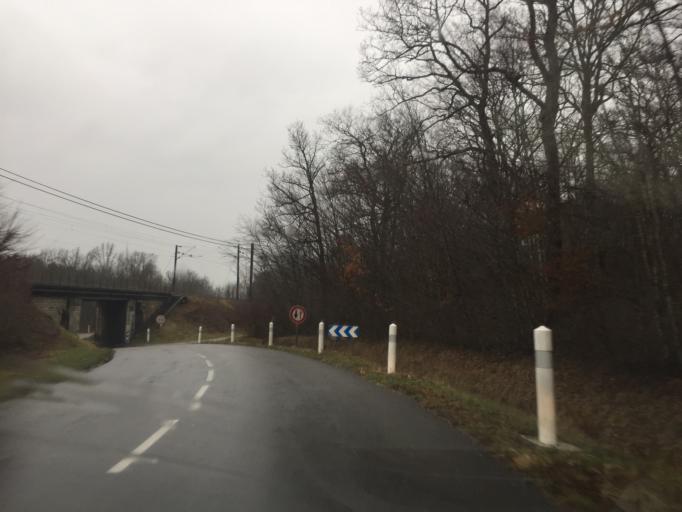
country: FR
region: Franche-Comte
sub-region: Departement du Jura
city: Mouchard
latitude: 46.9957
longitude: 5.7913
